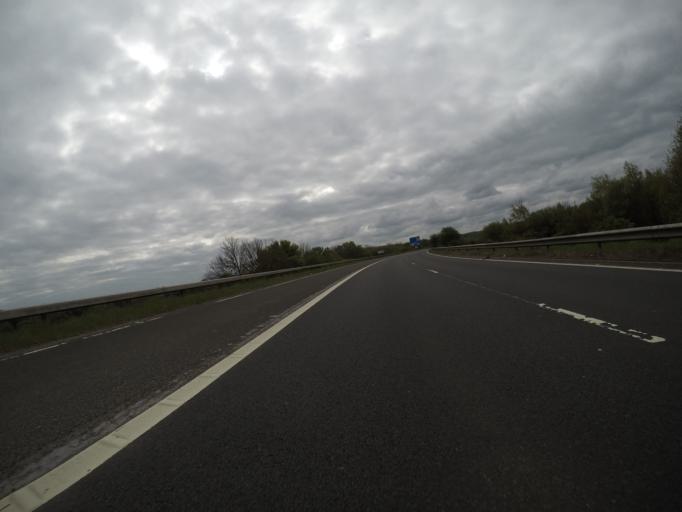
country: GB
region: Scotland
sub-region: Edinburgh
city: Kirkliston
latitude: 55.9449
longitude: -3.4039
